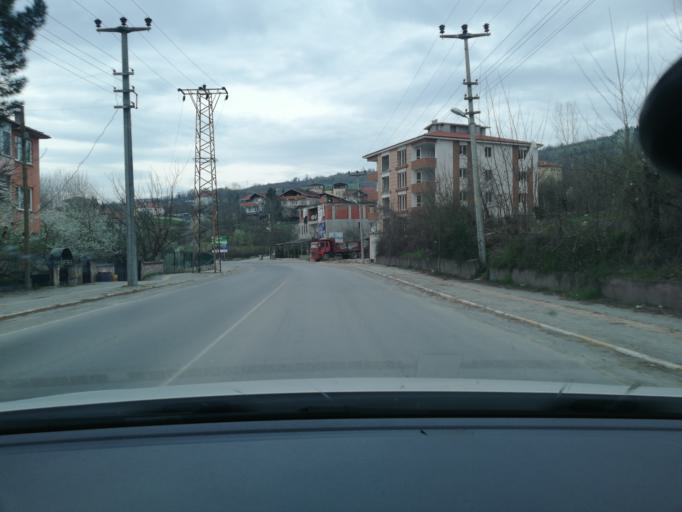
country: TR
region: Zonguldak
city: Gokcebey
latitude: 41.3096
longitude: 32.1324
